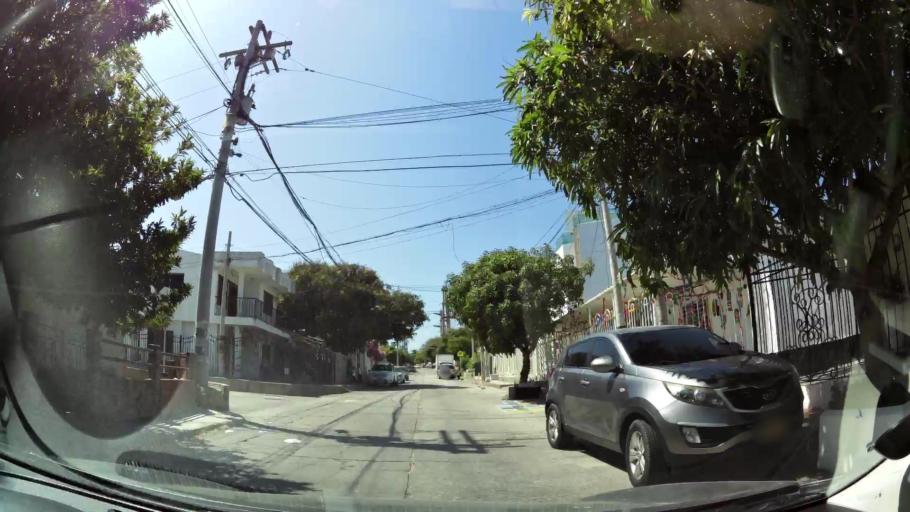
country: CO
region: Atlantico
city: Barranquilla
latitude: 11.0068
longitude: -74.7917
